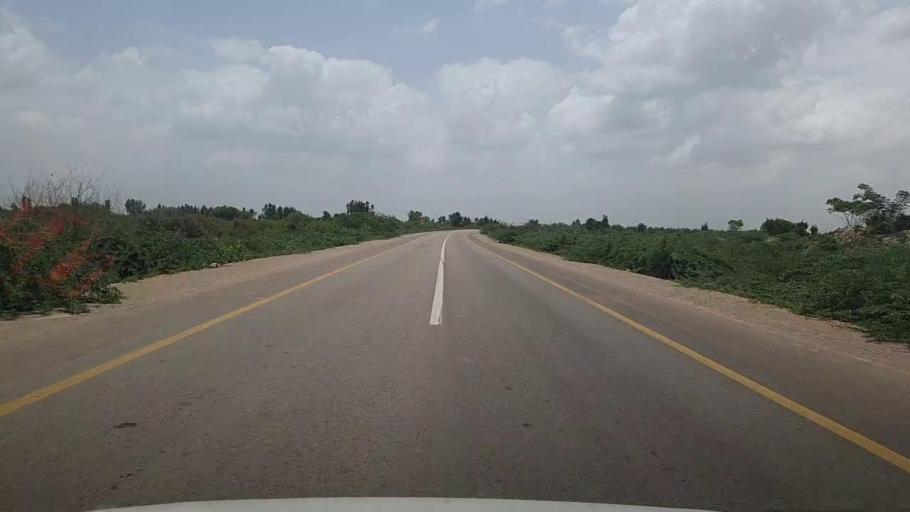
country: PK
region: Sindh
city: Thatta
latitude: 24.7430
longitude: 67.9495
